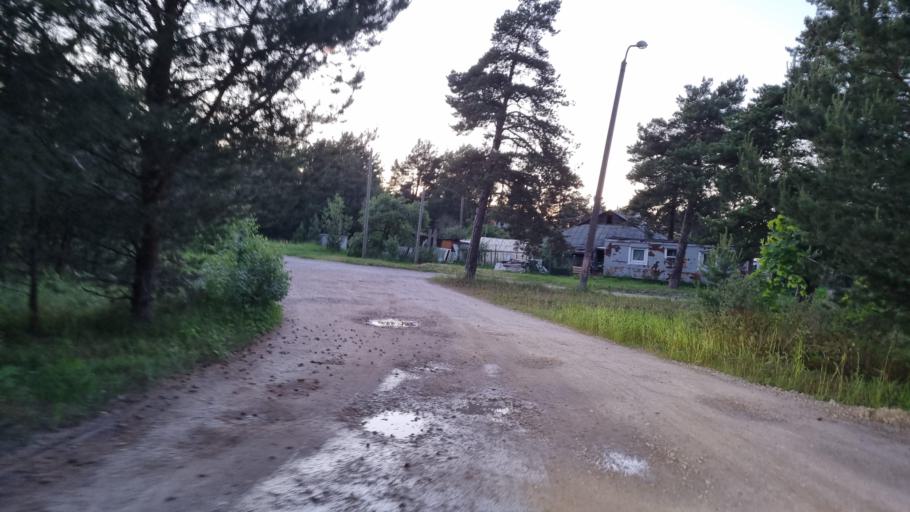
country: LV
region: Riga
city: Daugavgriva
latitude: 57.0230
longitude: 24.0291
